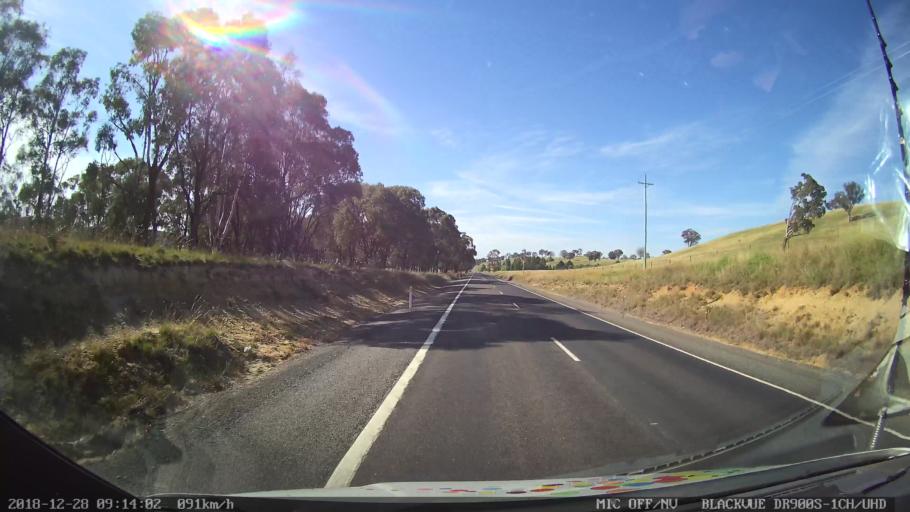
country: AU
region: New South Wales
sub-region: Upper Lachlan Shire
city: Crookwell
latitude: -34.2768
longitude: 149.3451
